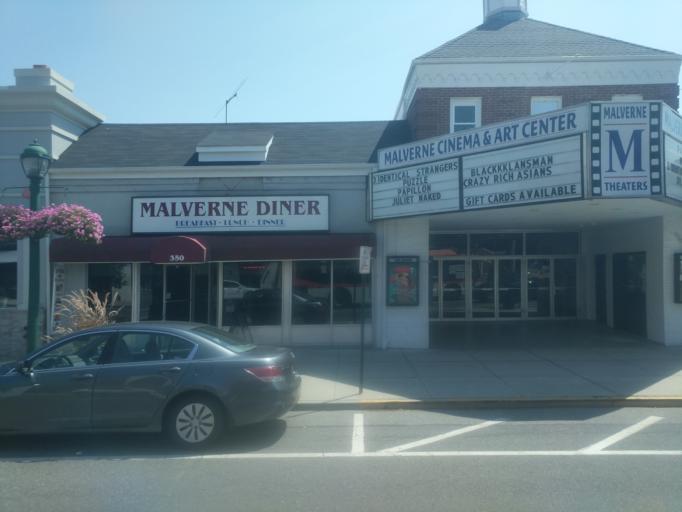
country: US
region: New York
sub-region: Nassau County
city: Malverne
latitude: 40.6774
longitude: -73.6679
